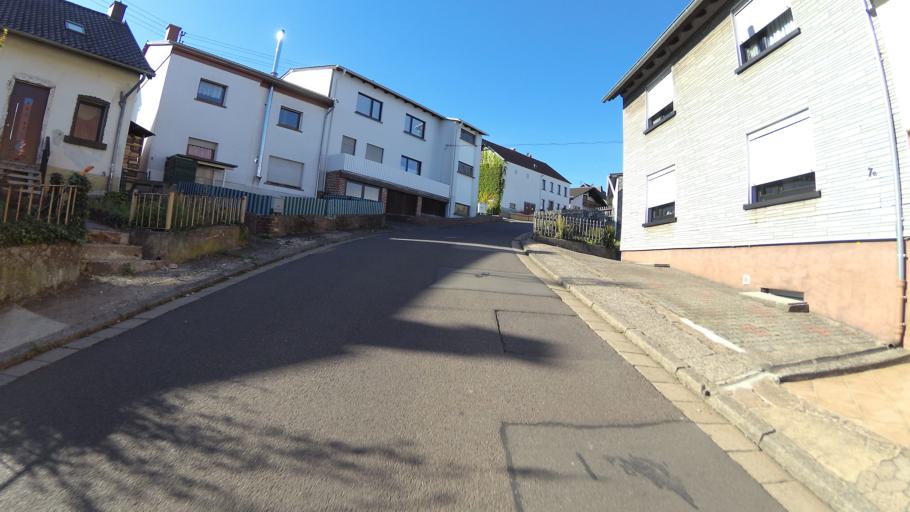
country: DE
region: Saarland
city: Eppelborn
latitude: 49.4100
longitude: 6.9628
